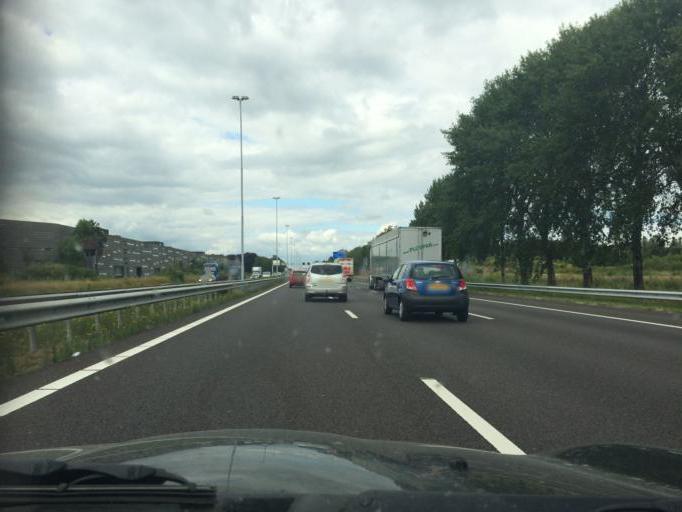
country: NL
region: North Brabant
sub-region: Gemeente Goirle
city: Goirle
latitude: 51.5368
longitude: 5.0753
